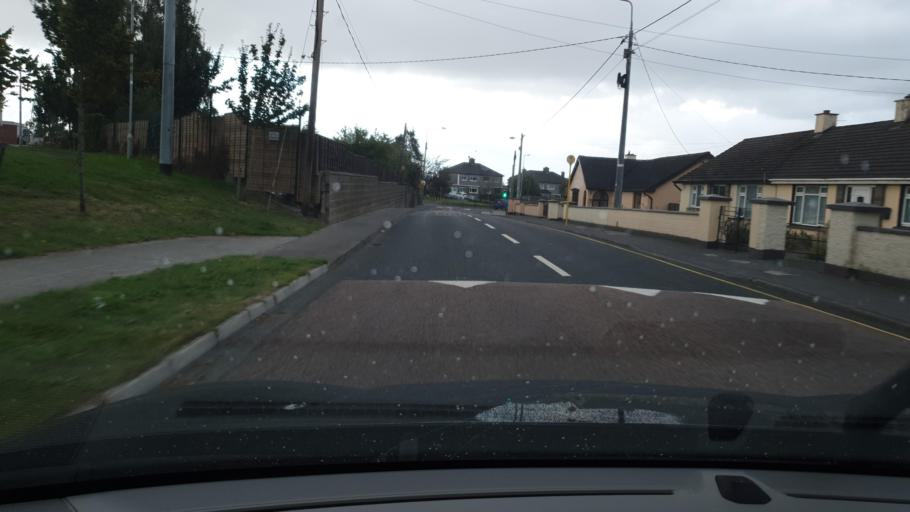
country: IE
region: Leinster
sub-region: South Dublin
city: Rathcoole
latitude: 53.2792
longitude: -6.4777
